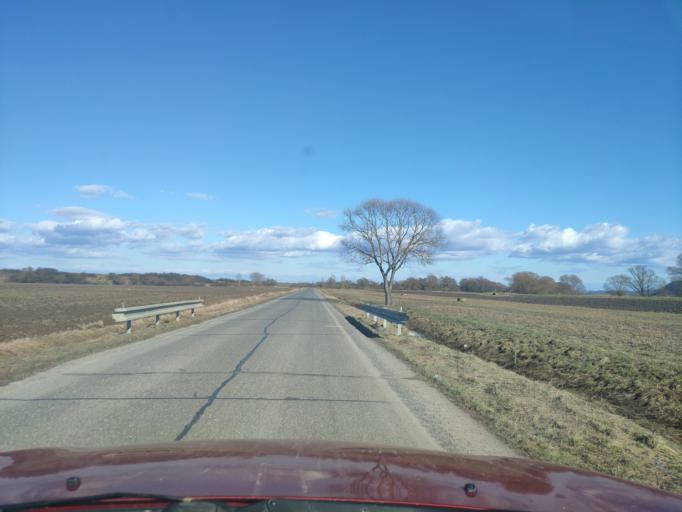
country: SK
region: Banskobystricky
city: Rimavska Sobota
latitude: 48.2814
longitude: 20.1206
